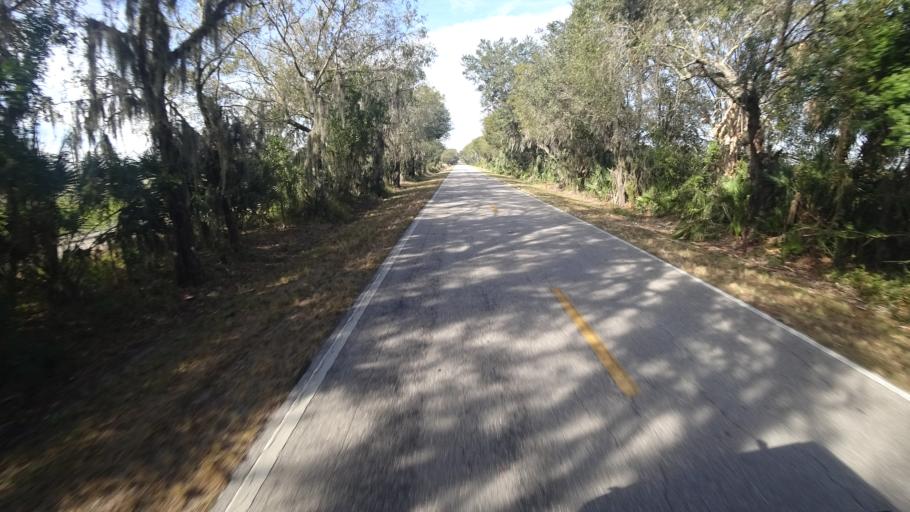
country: US
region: Florida
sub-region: Hillsborough County
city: Ruskin
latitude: 27.6232
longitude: -82.4577
